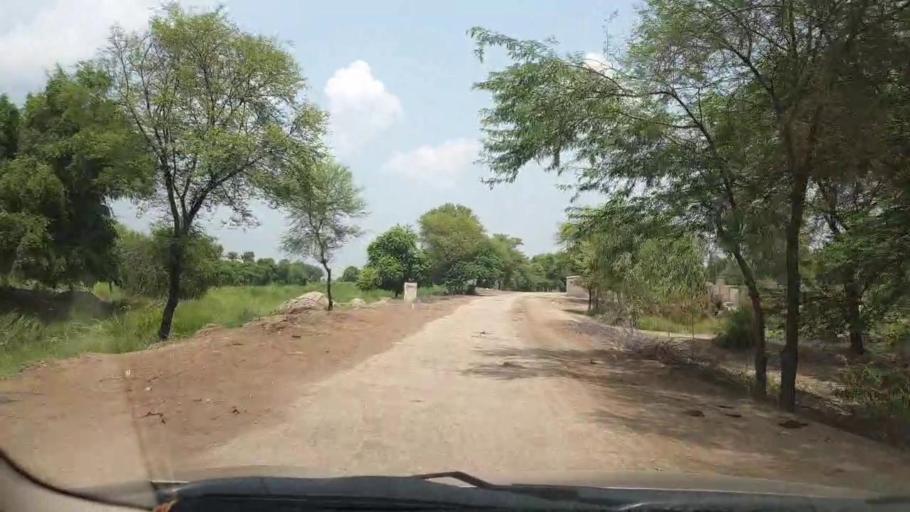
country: PK
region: Sindh
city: Larkana
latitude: 27.5976
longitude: 68.1399
